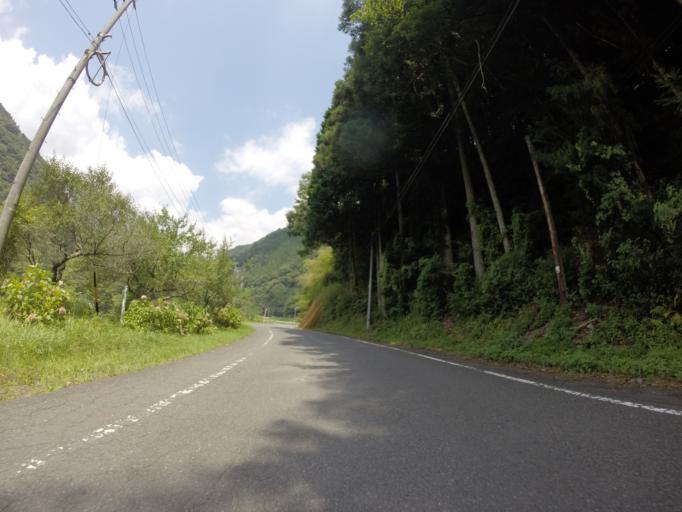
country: JP
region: Shizuoka
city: Shizuoka-shi
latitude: 35.2471
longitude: 138.3439
